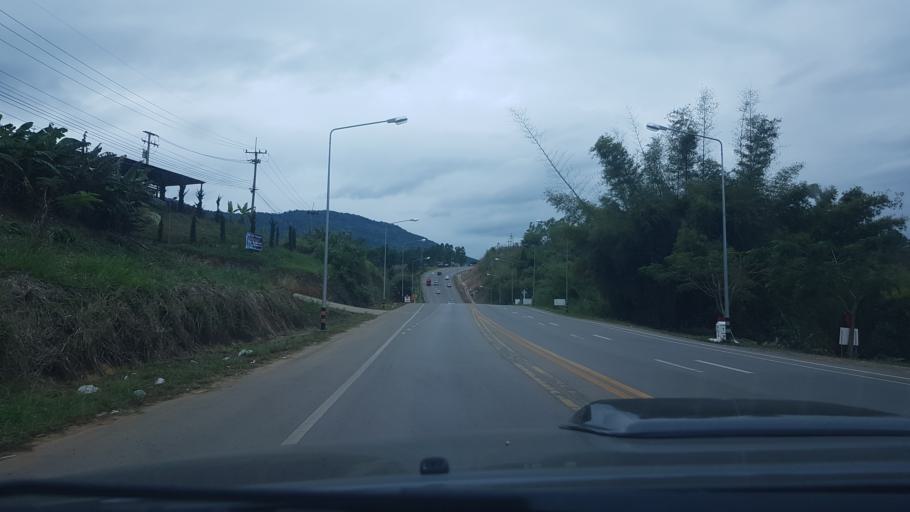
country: TH
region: Phetchabun
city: Khao Kho
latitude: 16.5703
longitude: 100.9967
